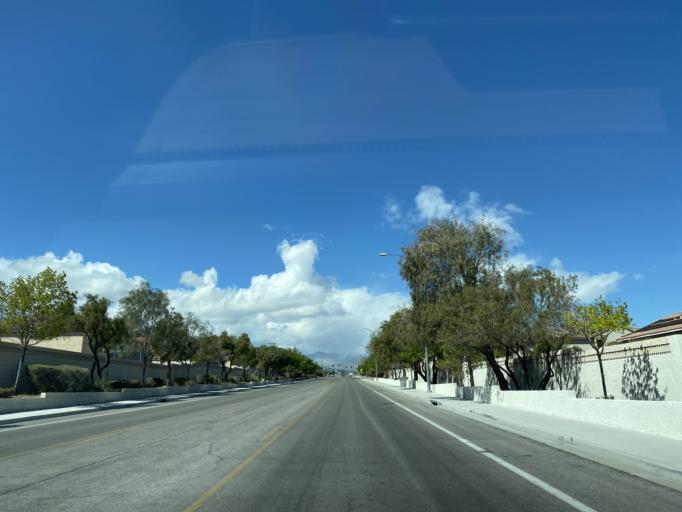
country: US
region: Nevada
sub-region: Clark County
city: Summerlin South
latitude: 36.3214
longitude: -115.2930
